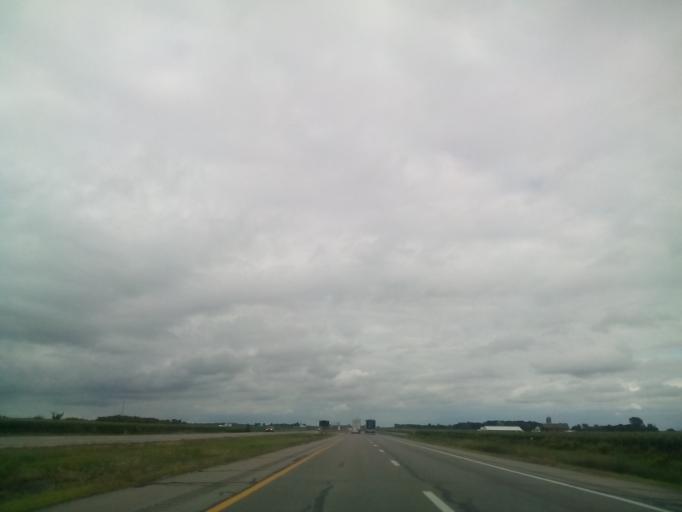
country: US
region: Ohio
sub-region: Fulton County
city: Burlington
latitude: 41.5904
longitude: -84.2860
